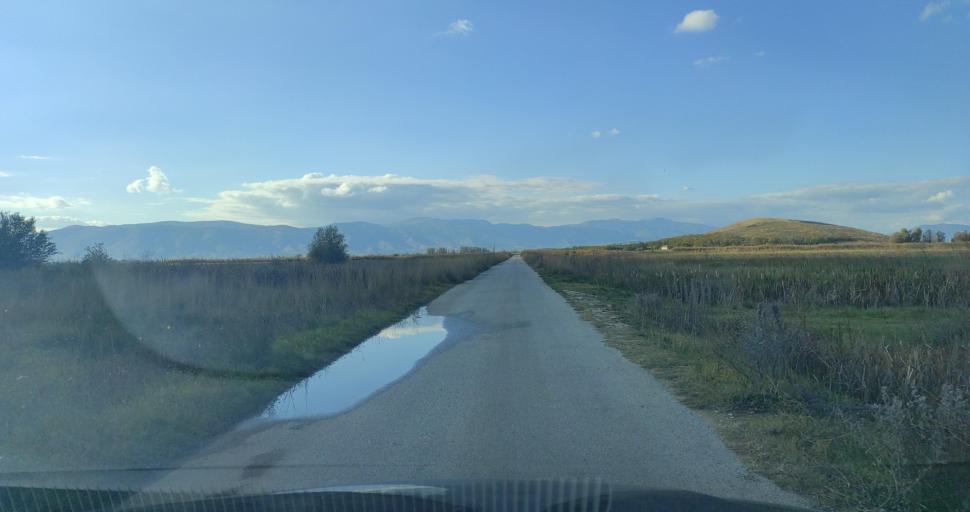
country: MK
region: Prilep
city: Topolcani
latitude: 41.2794
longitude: 21.4272
